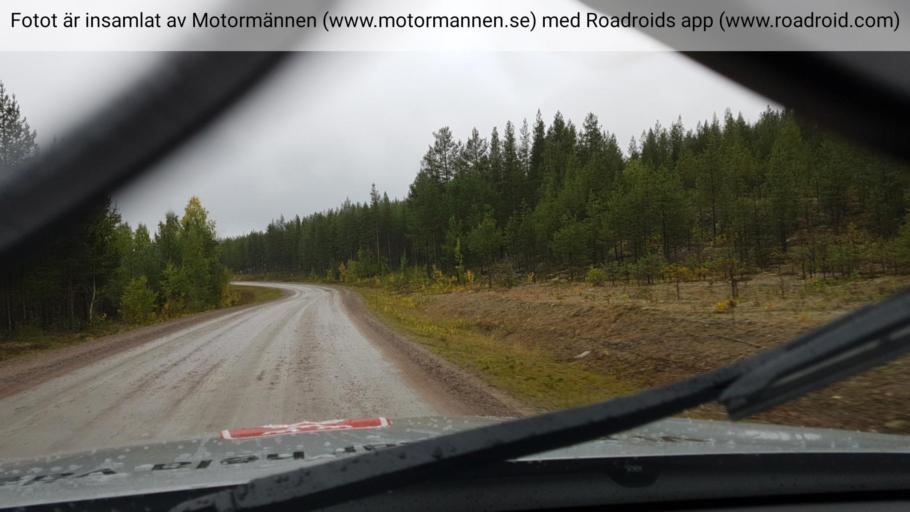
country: SE
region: Norrbotten
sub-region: Alvsbyns Kommun
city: AElvsbyn
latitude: 66.2718
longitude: 21.0897
